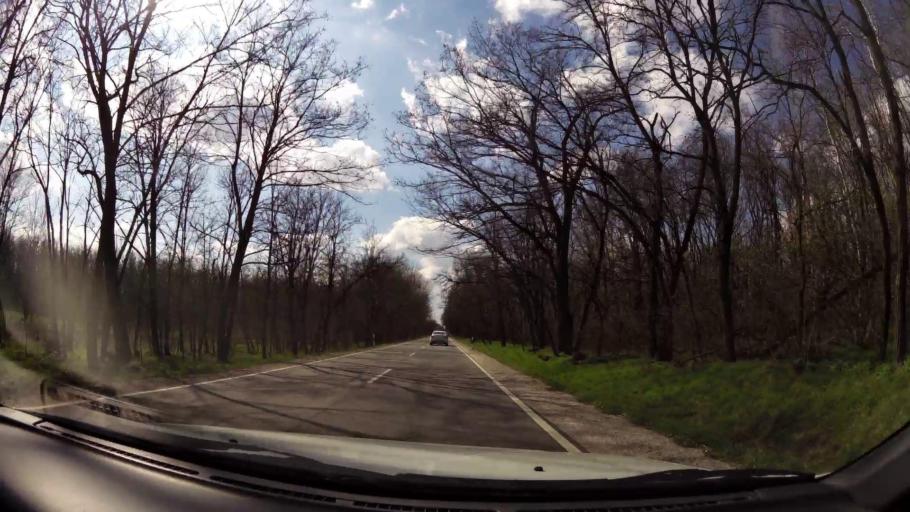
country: HU
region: Pest
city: Forropuszta
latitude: 47.4636
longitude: 19.6383
